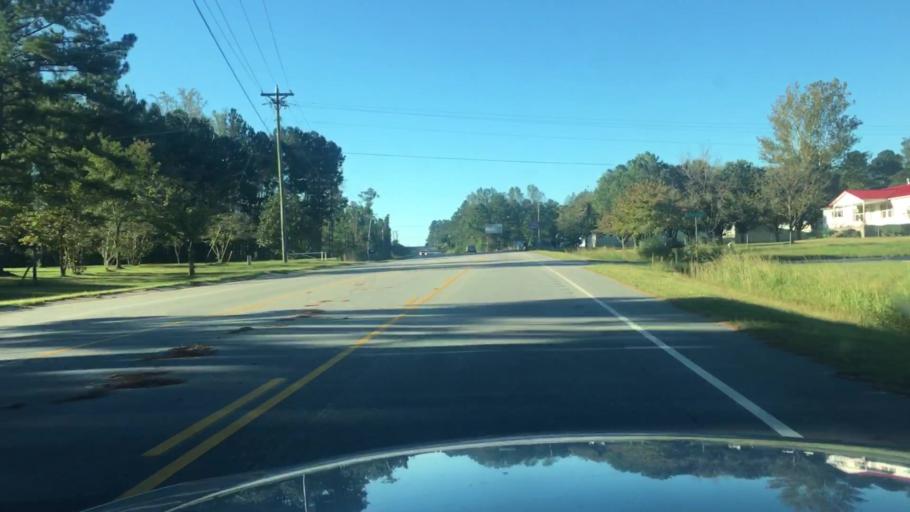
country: US
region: North Carolina
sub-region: Cumberland County
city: Spring Lake
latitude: 35.2535
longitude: -78.9268
